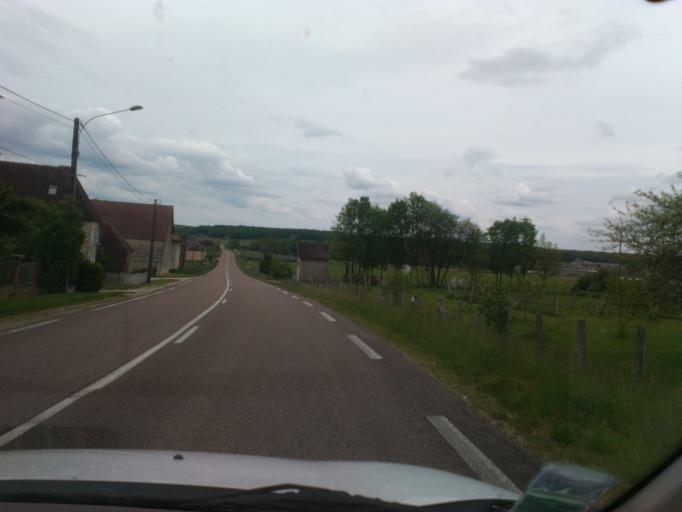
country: FR
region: Champagne-Ardenne
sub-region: Departement de l'Aube
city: Vendeuvre-sur-Barse
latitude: 48.2363
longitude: 4.3890
